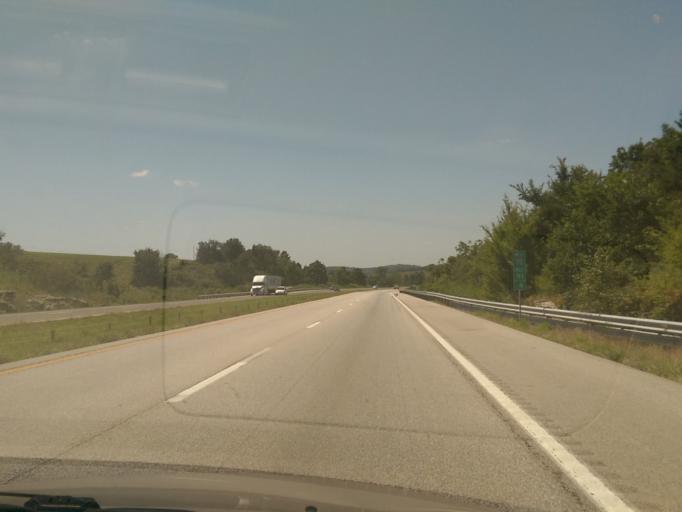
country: US
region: Missouri
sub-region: Cooper County
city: Boonville
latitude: 38.9335
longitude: -92.9697
